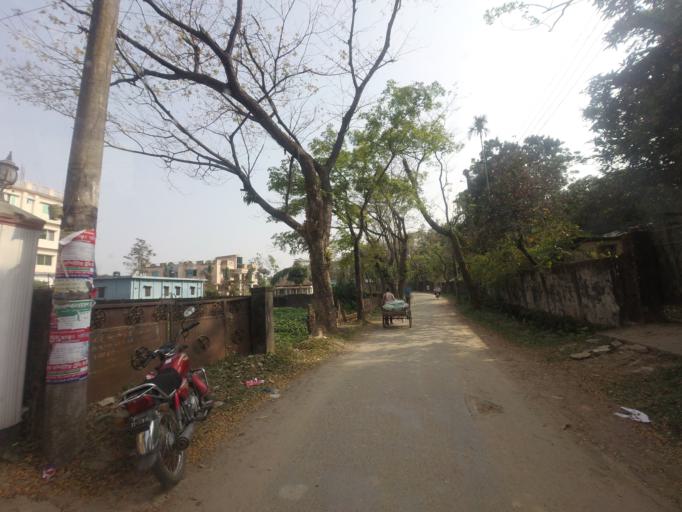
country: BD
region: Sylhet
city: Sylhet
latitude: 24.9123
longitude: 91.9409
